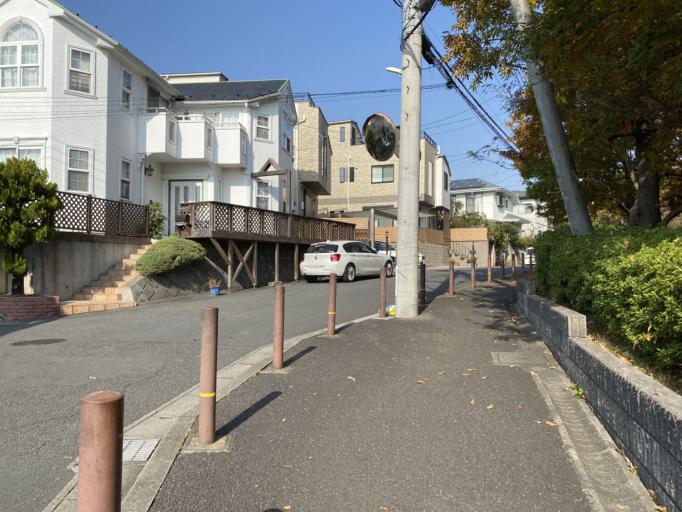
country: JP
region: Tokyo
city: Chofugaoka
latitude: 35.6086
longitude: 139.5028
